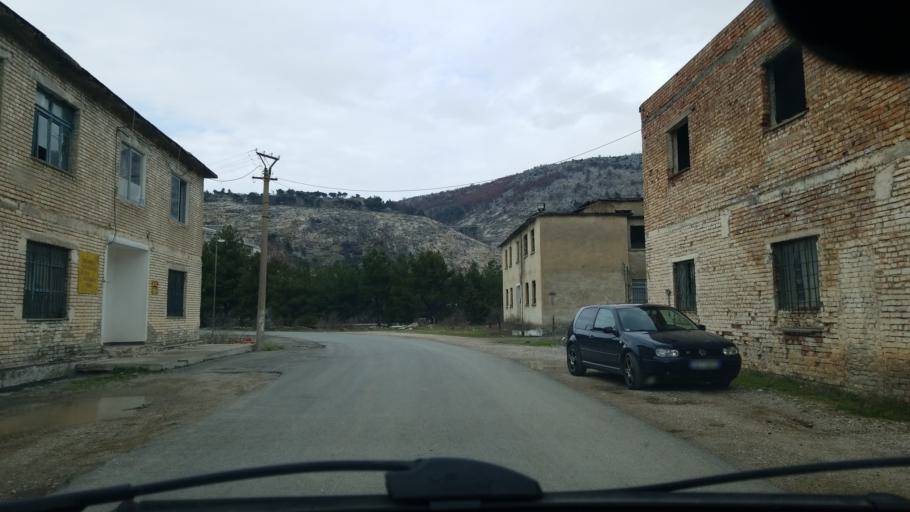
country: AL
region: Lezhe
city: Shengjin
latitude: 41.8107
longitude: 19.5850
